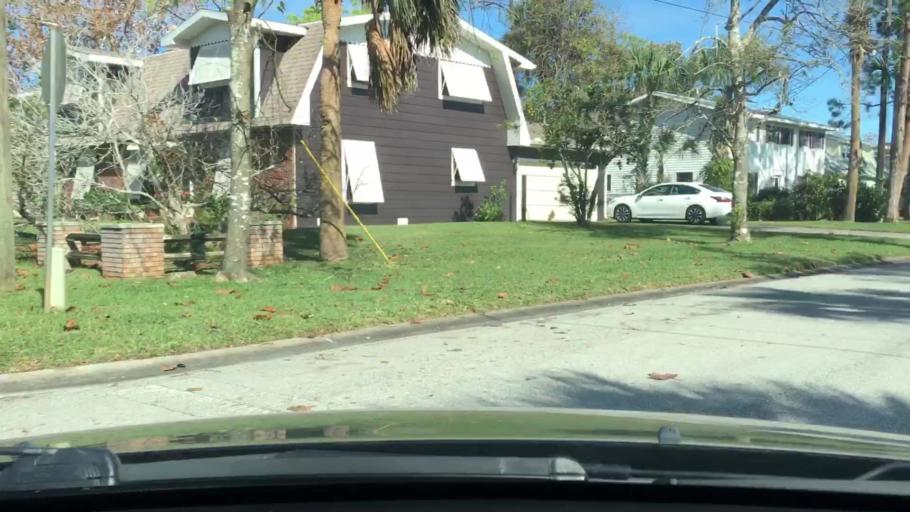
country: US
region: Florida
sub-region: Volusia County
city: Ormond Beach
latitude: 29.2934
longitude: -81.0700
